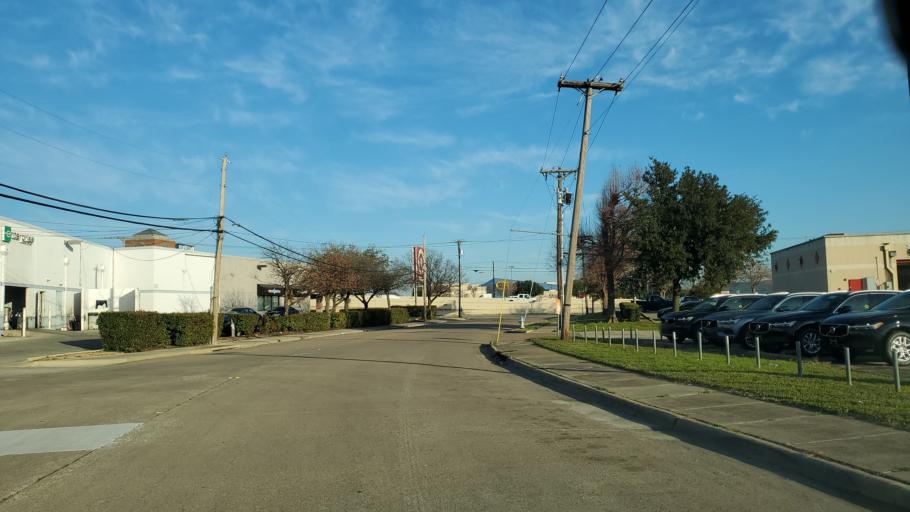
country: US
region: Texas
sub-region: Collin County
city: Plano
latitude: 33.0363
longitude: -96.7069
